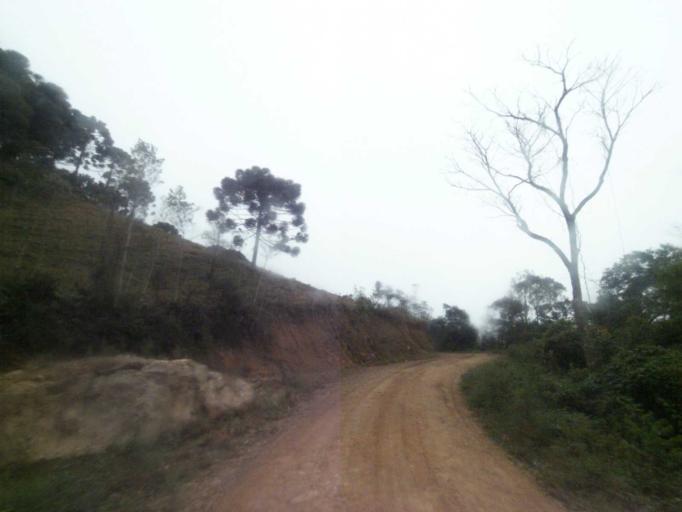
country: BR
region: Santa Catarina
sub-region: Anitapolis
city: Anitapolis
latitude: -27.8557
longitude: -49.1342
